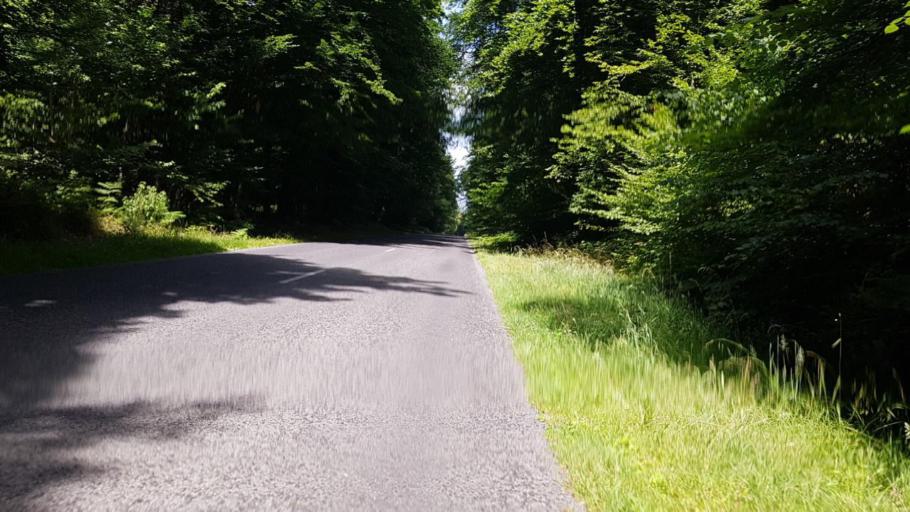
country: FR
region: Picardie
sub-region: Departement de l'Oise
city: Chiry-Ourscamp
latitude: 49.5438
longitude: 2.9860
